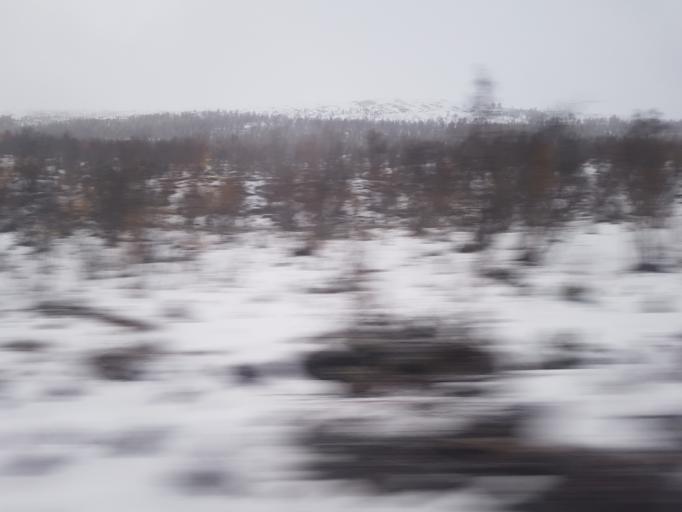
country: NO
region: Oppland
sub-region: Dovre
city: Dovre
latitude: 62.1760
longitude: 9.4504
